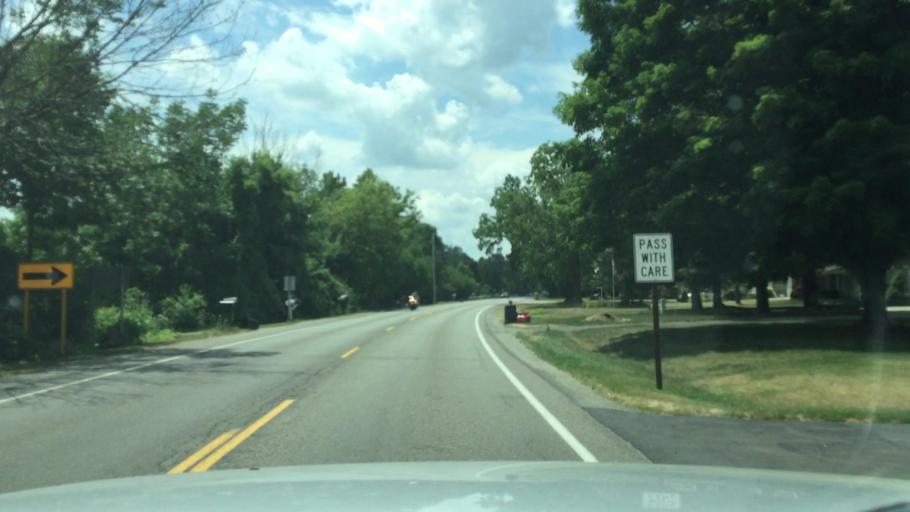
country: US
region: Michigan
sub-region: Genesee County
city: Flushing
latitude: 43.0851
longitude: -83.8669
